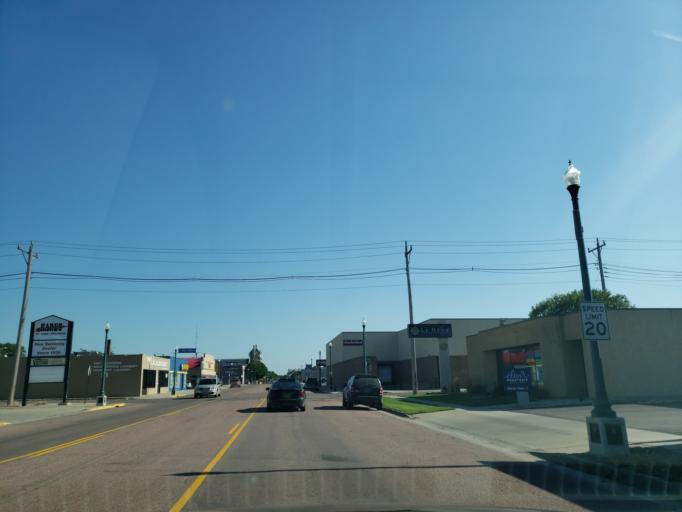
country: US
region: South Dakota
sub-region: Davison County
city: Mitchell
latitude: 43.7182
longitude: -98.0256
